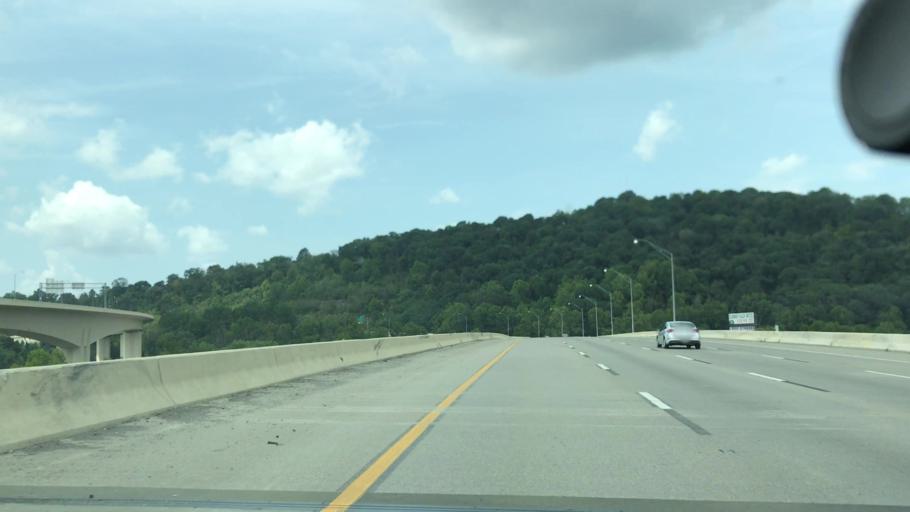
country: US
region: West Virginia
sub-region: Kanawha County
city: South Charleston
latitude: 38.3608
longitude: -81.7171
